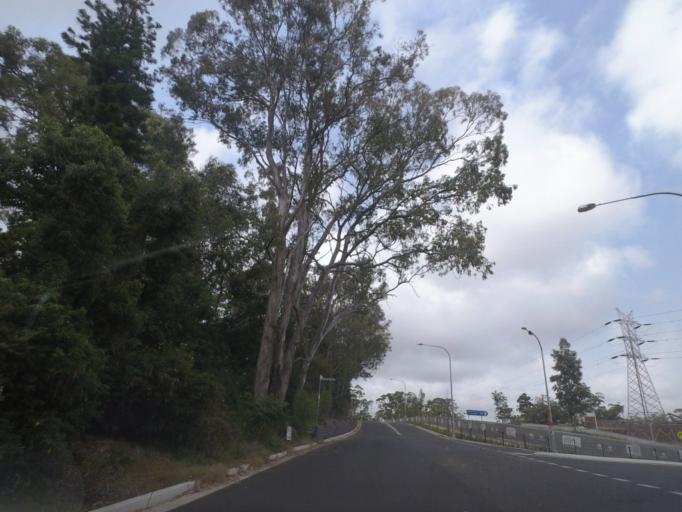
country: AU
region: New South Wales
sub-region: The Hills Shire
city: West Pennant
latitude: -33.7369
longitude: 151.0348
